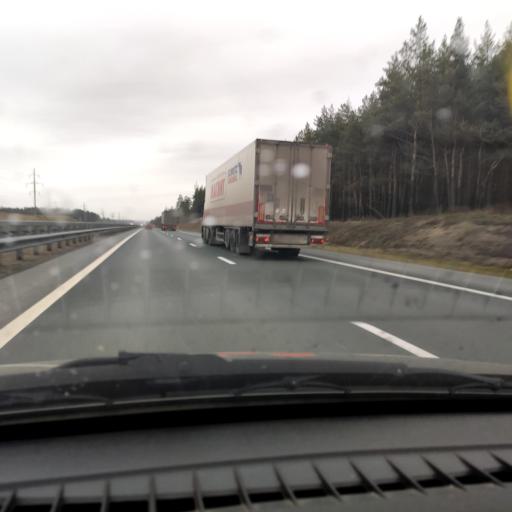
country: RU
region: Samara
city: Povolzhskiy
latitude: 53.5169
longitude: 49.7336
